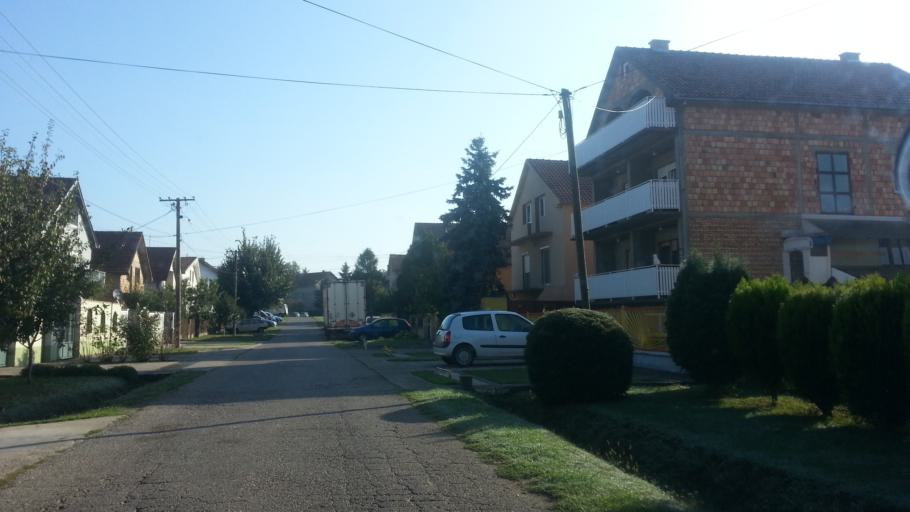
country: RS
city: Stari Banovci
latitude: 44.9801
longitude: 20.2741
